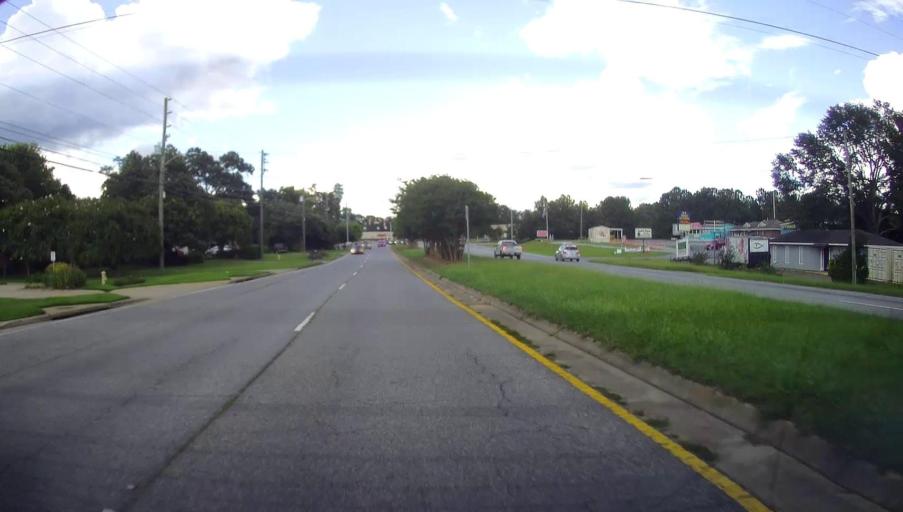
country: US
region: Georgia
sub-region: Muscogee County
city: Columbus
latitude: 32.5267
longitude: -84.9264
